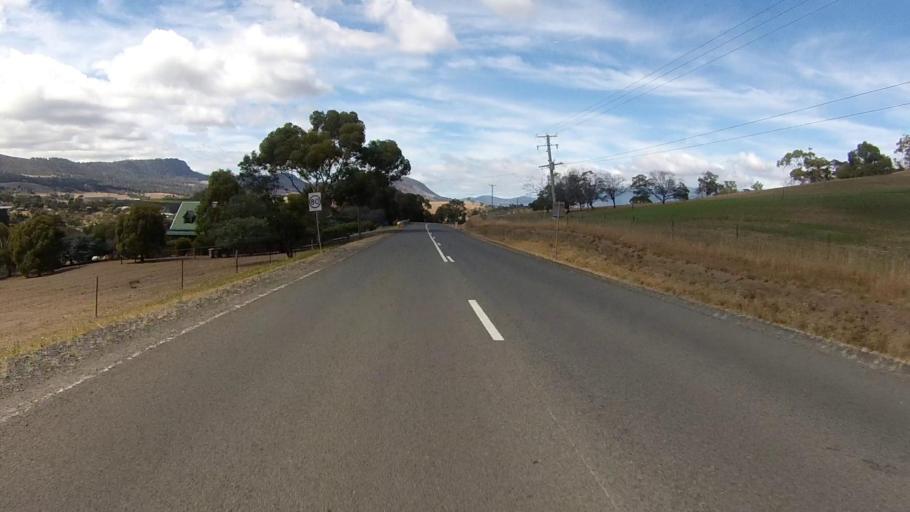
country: AU
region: Tasmania
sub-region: Brighton
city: Old Beach
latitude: -42.7322
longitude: 147.2889
